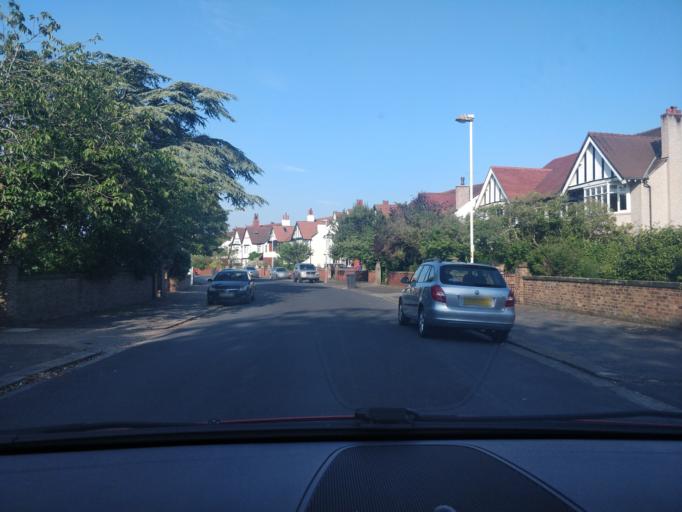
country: GB
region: England
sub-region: Sefton
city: Southport
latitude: 53.6553
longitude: -2.9811
